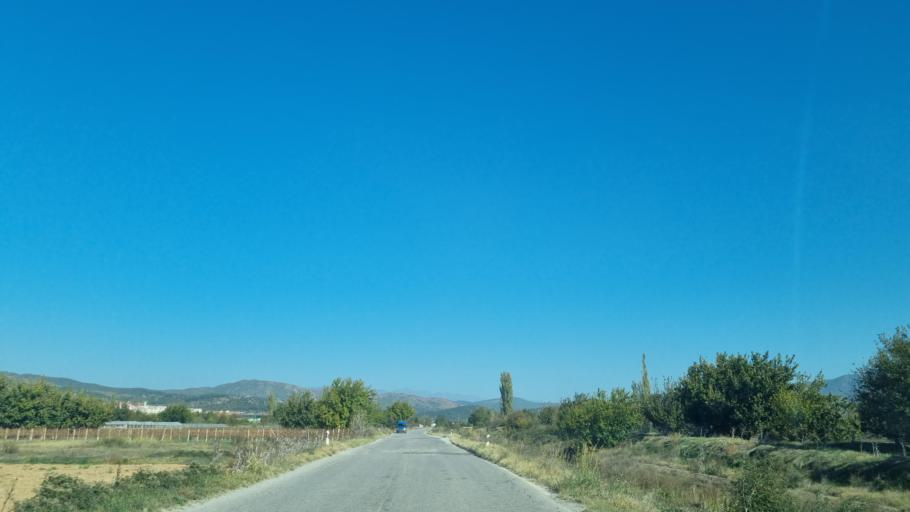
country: MK
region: Bogdanci
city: Bogdanci
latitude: 41.1905
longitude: 22.5635
